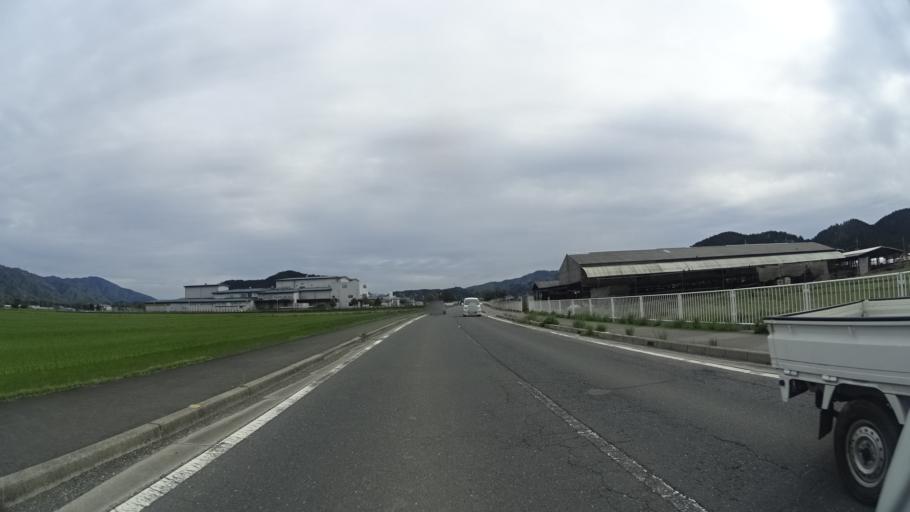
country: JP
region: Kyoto
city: Kameoka
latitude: 35.0881
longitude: 135.5370
